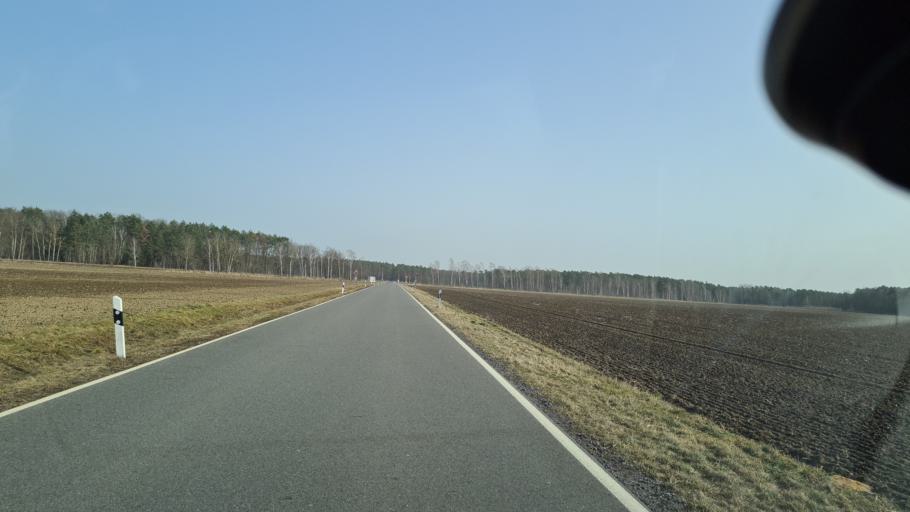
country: DE
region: Brandenburg
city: Cottbus
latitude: 51.6982
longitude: 14.3939
